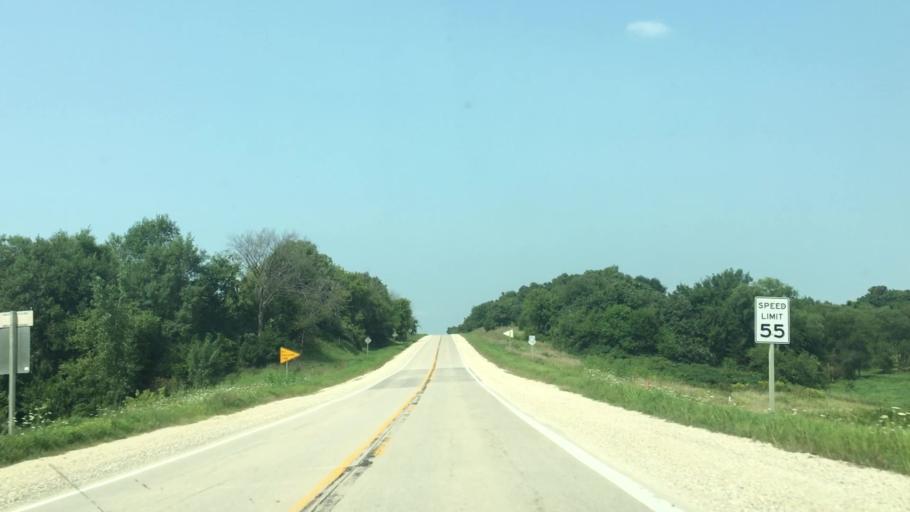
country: US
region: Iowa
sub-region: Fayette County
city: West Union
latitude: 43.1208
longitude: -91.8699
